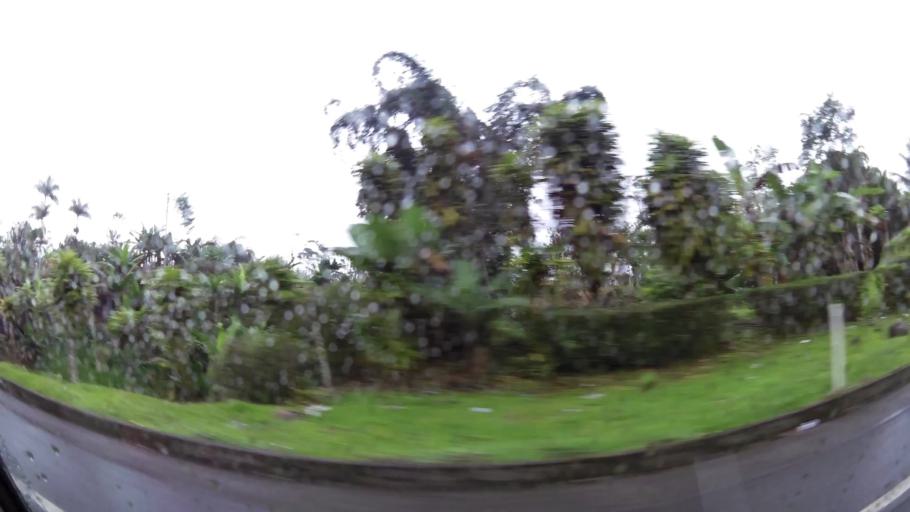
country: EC
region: Santo Domingo de los Tsachilas
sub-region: Canton Santo Domingo de los Colorados
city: Santo Domingo de los Colorados
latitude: -0.2260
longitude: -79.1241
